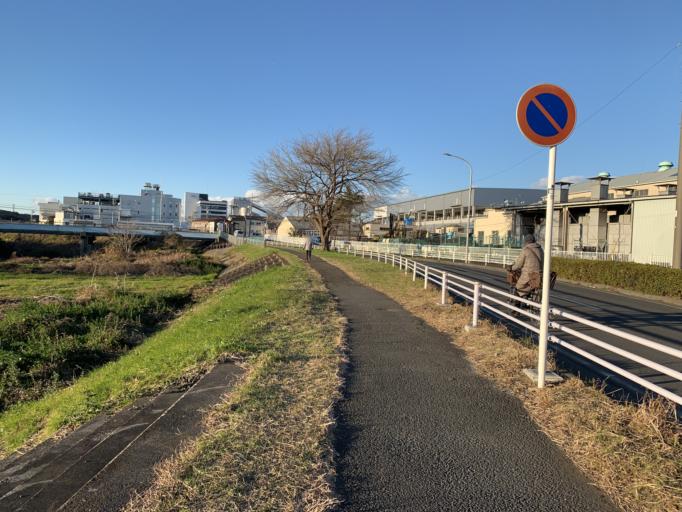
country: JP
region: Tokyo
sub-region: Machida-shi
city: Machida
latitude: 35.5177
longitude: 139.5521
